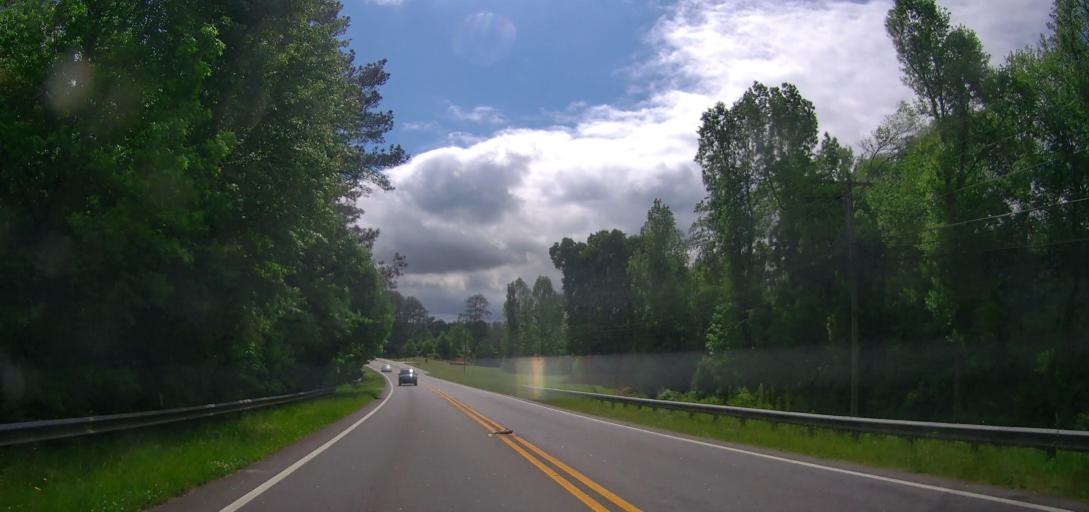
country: US
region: Georgia
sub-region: Rockdale County
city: Conyers
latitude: 33.6323
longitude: -84.0353
